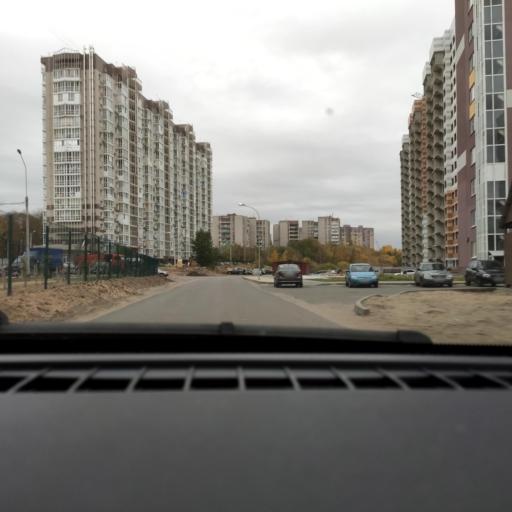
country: RU
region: Voronezj
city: Voronezh
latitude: 51.7147
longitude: 39.2694
